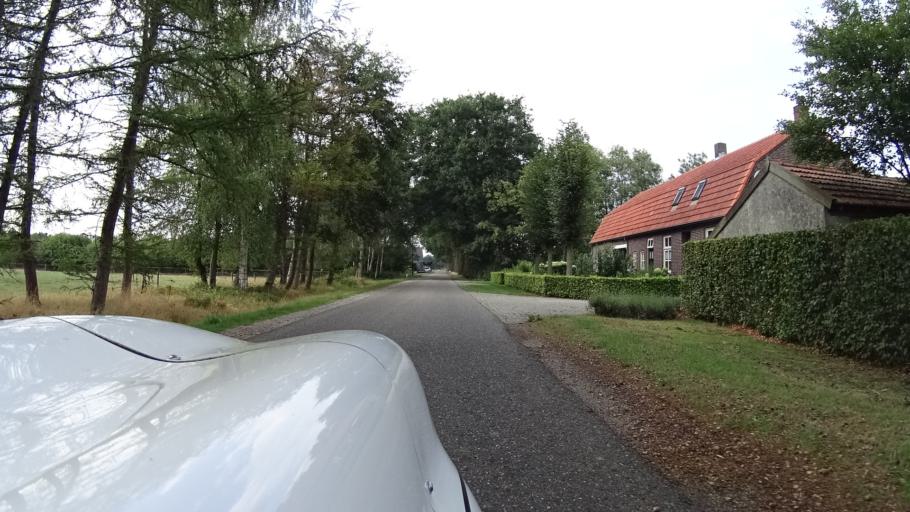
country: NL
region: North Brabant
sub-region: Gemeente Boekel
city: Boekel
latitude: 51.5924
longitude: 5.7204
